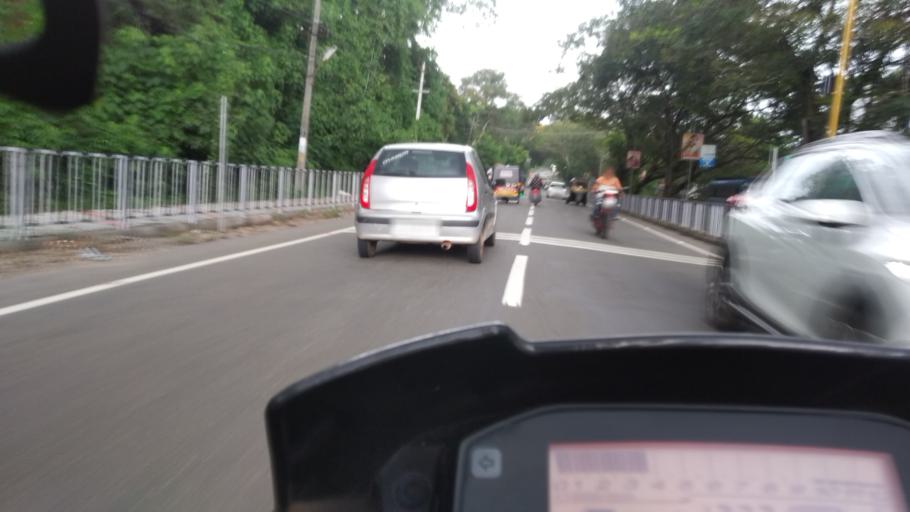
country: IN
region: Kerala
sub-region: Thiruvananthapuram
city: Attingal
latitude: 8.7079
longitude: 76.8144
